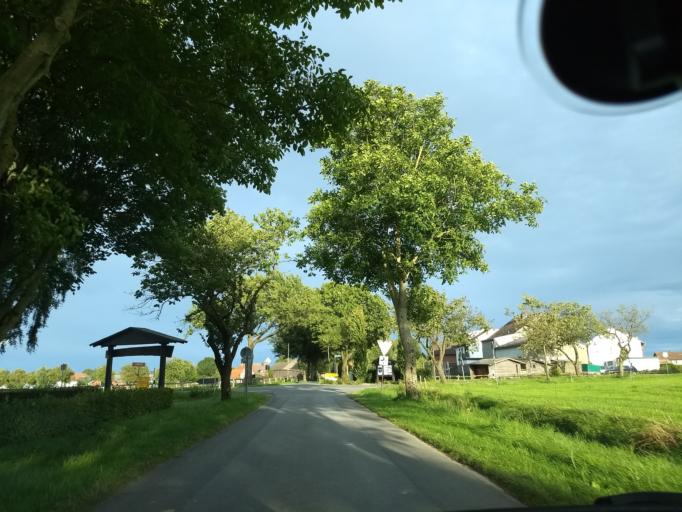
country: DE
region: North Rhine-Westphalia
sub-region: Regierungsbezirk Arnsberg
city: Ruthen
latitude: 51.5004
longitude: 8.5006
